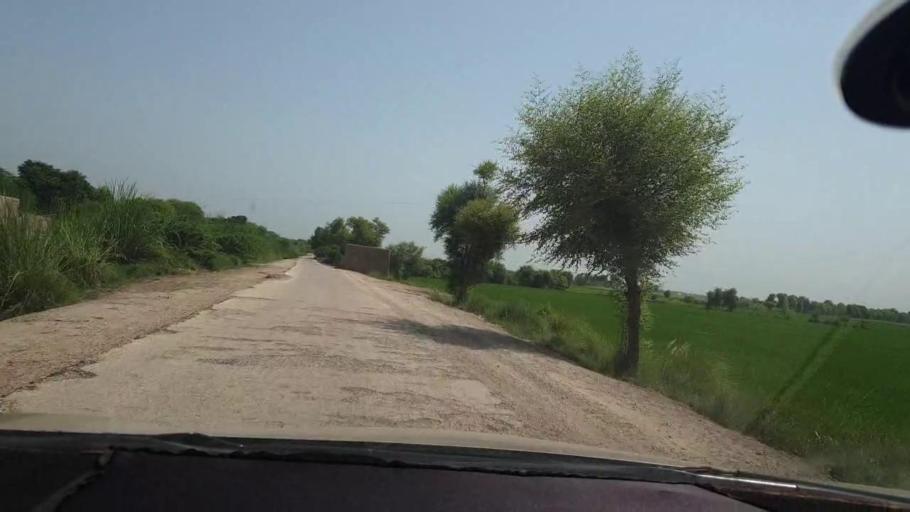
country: PK
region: Sindh
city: Kambar
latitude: 27.5216
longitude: 68.0081
